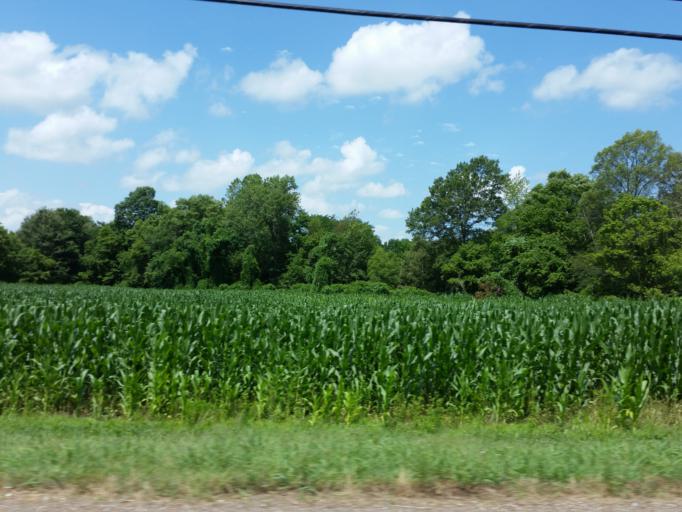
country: US
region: Tennessee
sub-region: Weakley County
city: Martin
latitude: 36.3640
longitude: -88.8501
